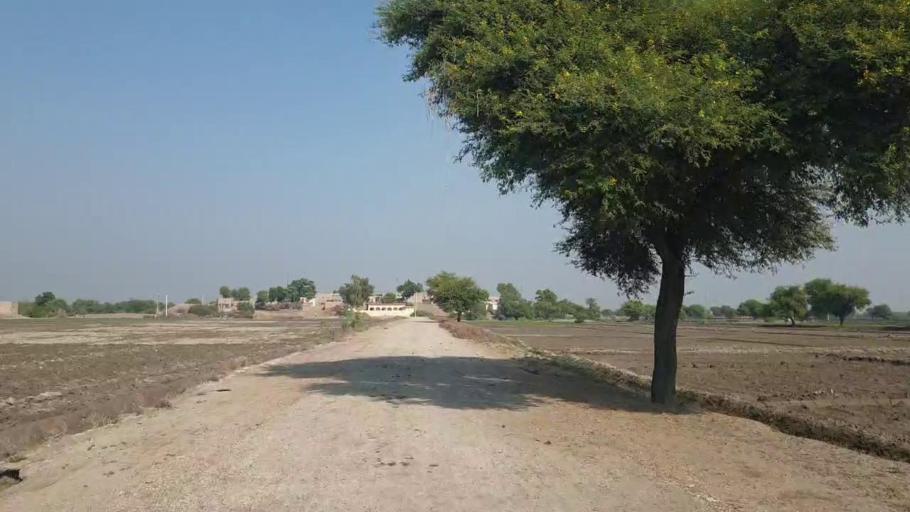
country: PK
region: Sindh
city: Sehwan
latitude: 26.4284
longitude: 67.7820
